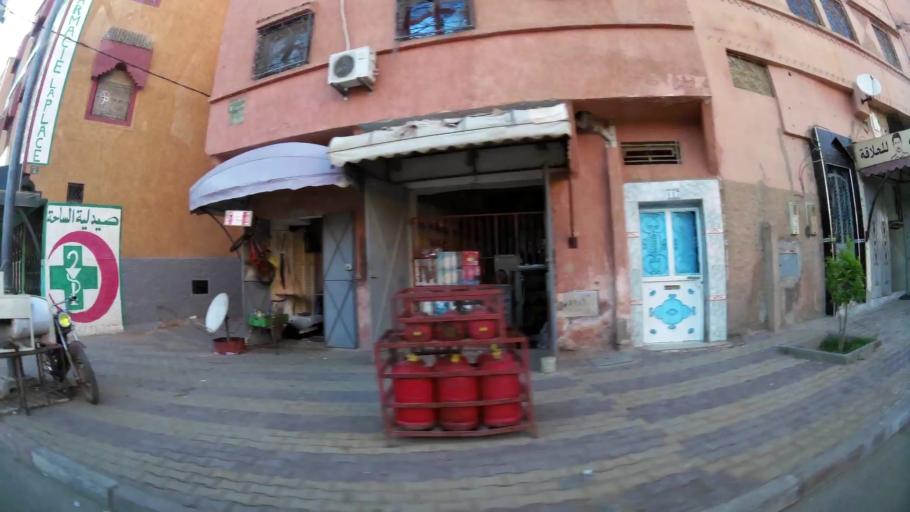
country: MA
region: Marrakech-Tensift-Al Haouz
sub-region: Kelaa-Des-Sraghna
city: Sidi Abdallah
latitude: 32.2452
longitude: -7.9519
